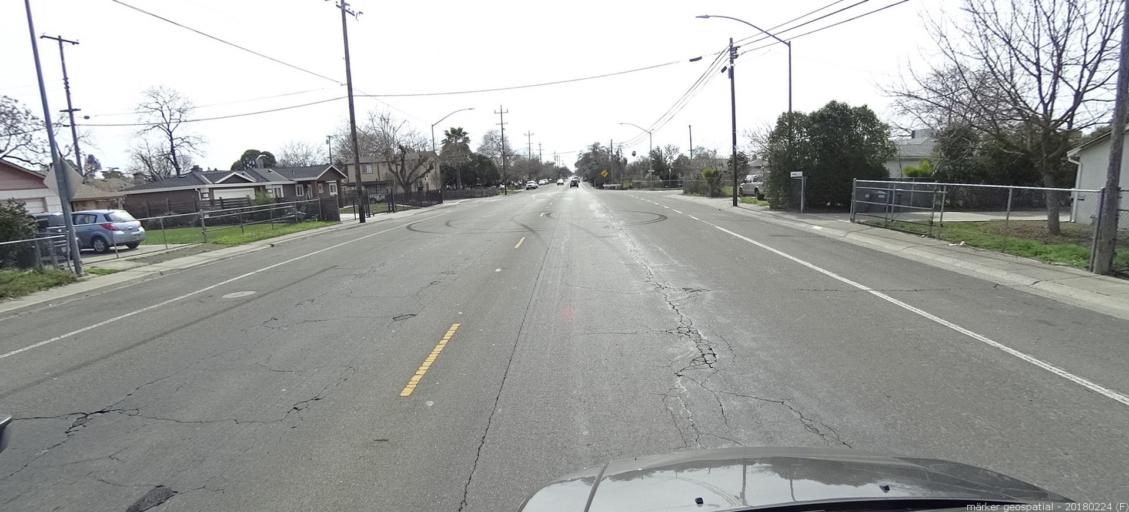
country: US
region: California
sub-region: Sacramento County
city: Rio Linda
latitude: 38.6974
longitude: -121.4569
